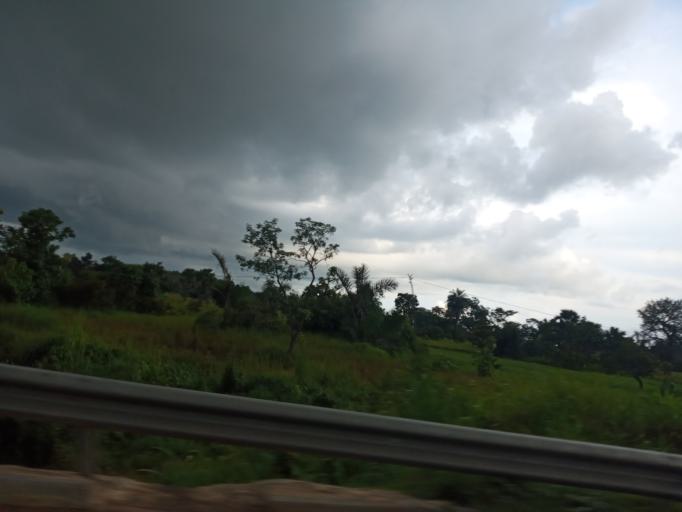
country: TG
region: Centrale
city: Sotouboua
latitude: 8.5988
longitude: 0.9987
